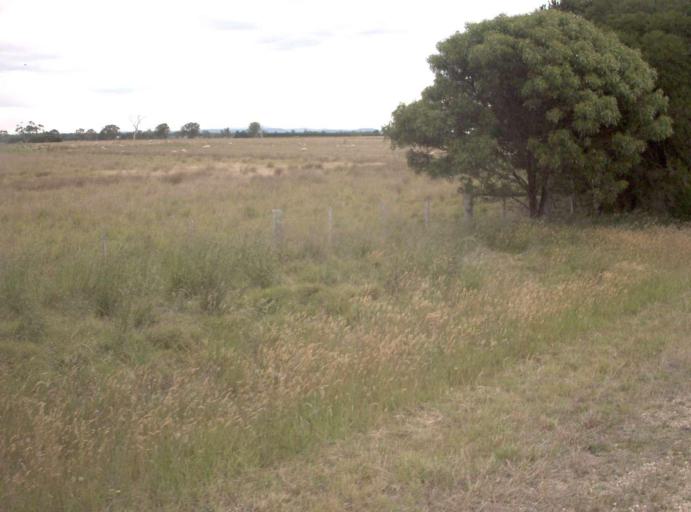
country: AU
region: Victoria
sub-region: East Gippsland
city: Bairnsdale
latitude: -37.9580
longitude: 147.5001
